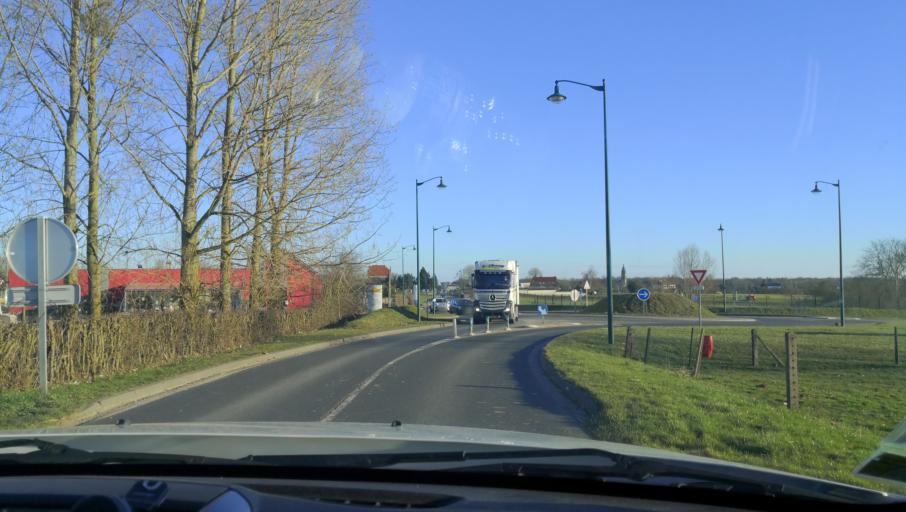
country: FR
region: Haute-Normandie
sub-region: Departement de la Seine-Maritime
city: Buchy
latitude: 49.5923
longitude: 1.3504
